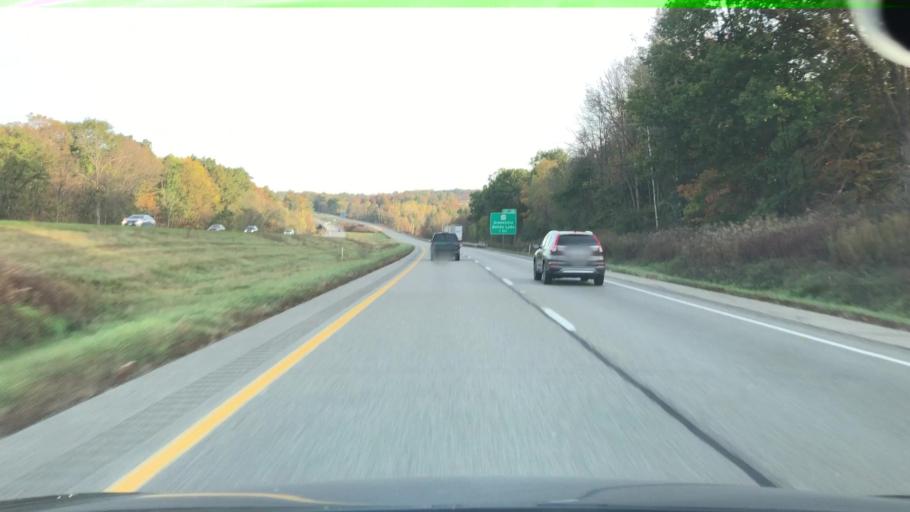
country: US
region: Pennsylvania
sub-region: Mercer County
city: Stoneboro
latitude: 41.3636
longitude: -80.1578
